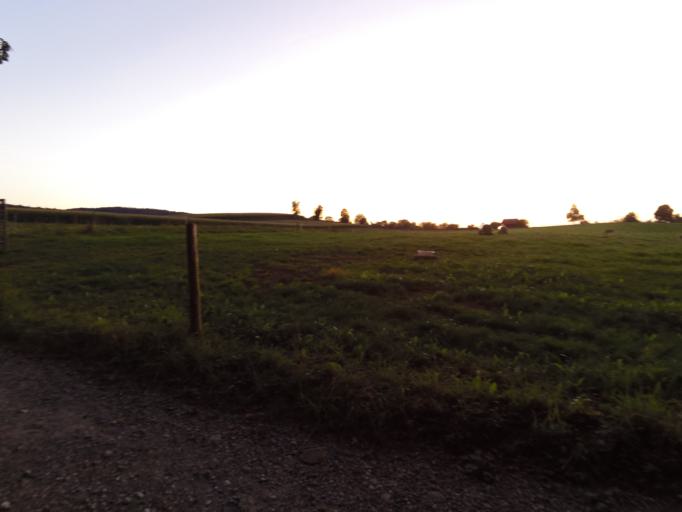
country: CH
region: Thurgau
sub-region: Weinfelden District
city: Wigoltingen
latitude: 47.5722
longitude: 9.0197
